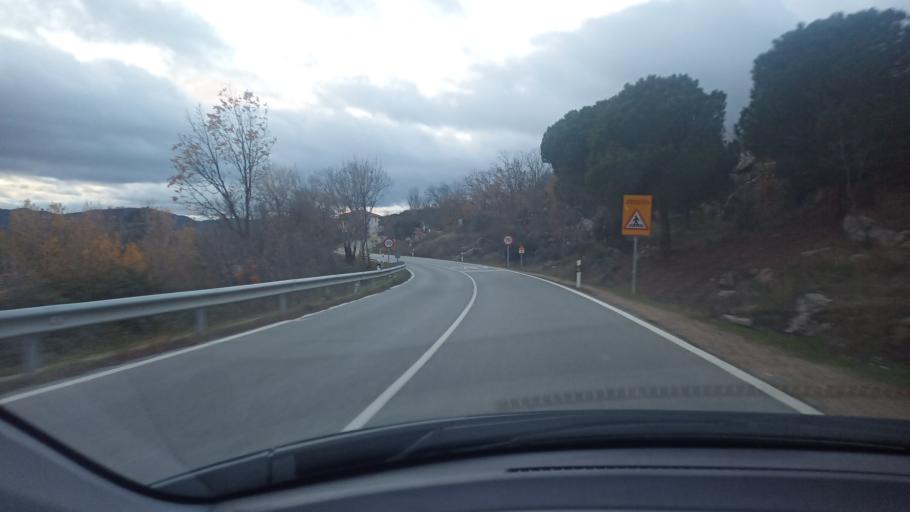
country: ES
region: Madrid
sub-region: Provincia de Madrid
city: Zarzalejo
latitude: 40.5403
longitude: -4.1531
